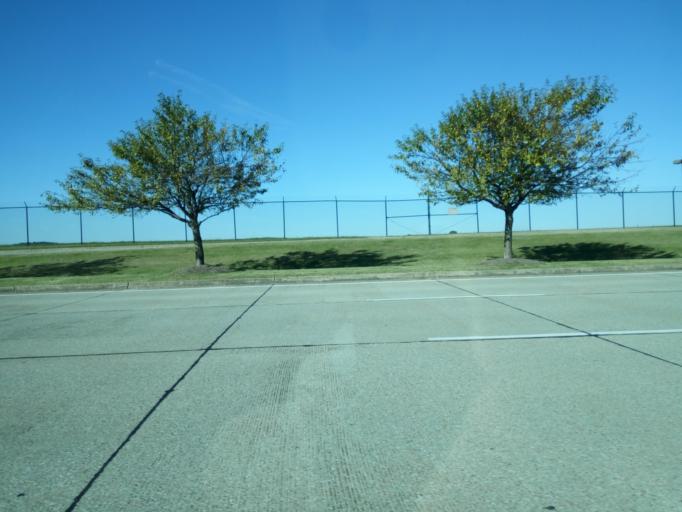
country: US
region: Kentucky
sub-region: Jefferson County
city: Audubon Park
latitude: 38.1865
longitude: -85.7462
